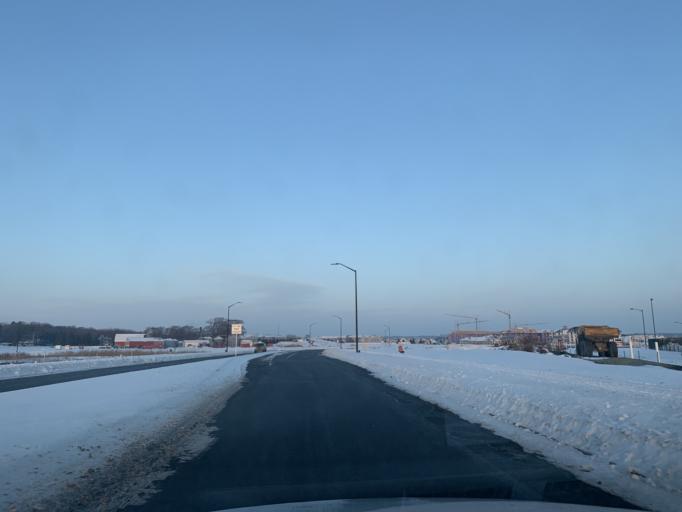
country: US
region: Minnesota
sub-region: Scott County
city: Shakopee
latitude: 44.7858
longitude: -93.4833
